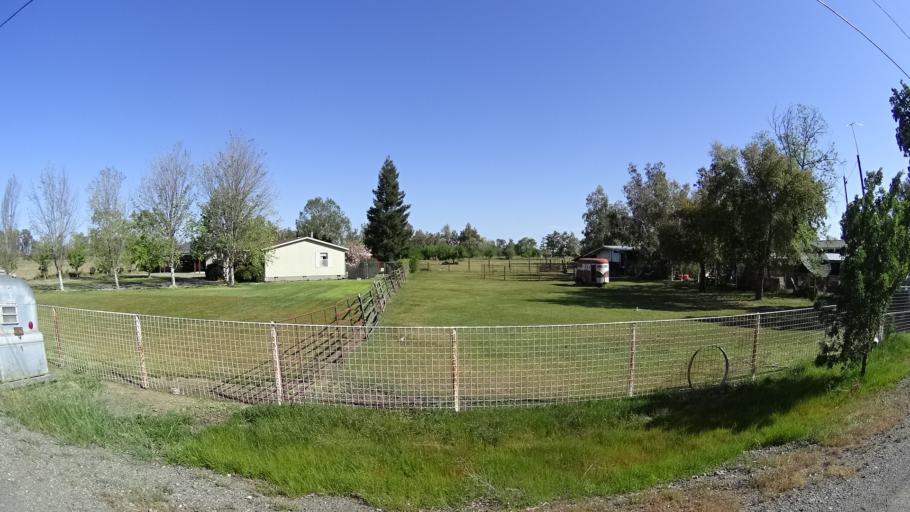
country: US
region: California
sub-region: Glenn County
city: Orland
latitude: 39.7289
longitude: -122.1590
